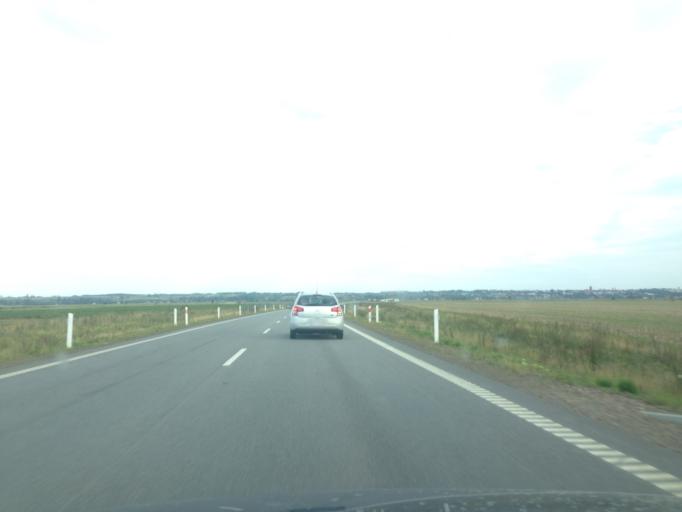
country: PL
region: Pomeranian Voivodeship
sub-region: Powiat kwidzynski
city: Kwidzyn
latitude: 53.7607
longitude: 18.8726
